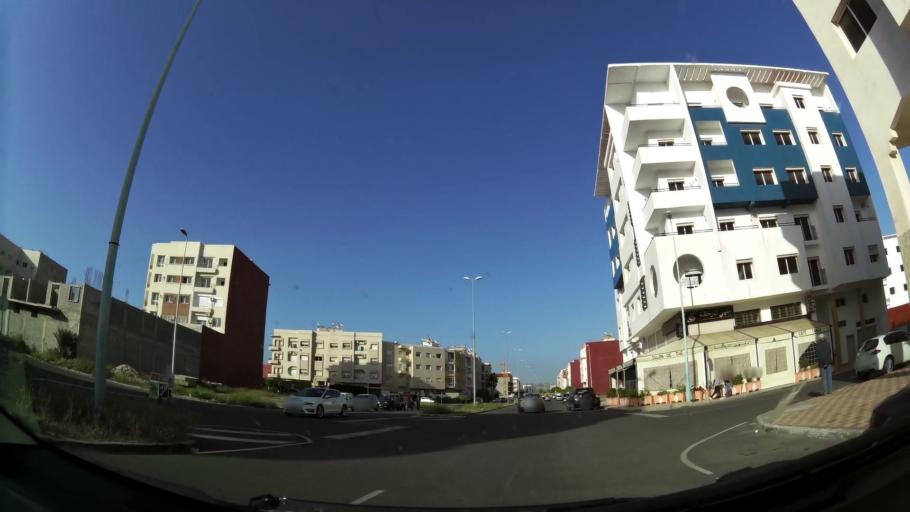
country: MA
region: Oued ed Dahab-Lagouira
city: Dakhla
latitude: 30.4002
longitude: -9.5350
